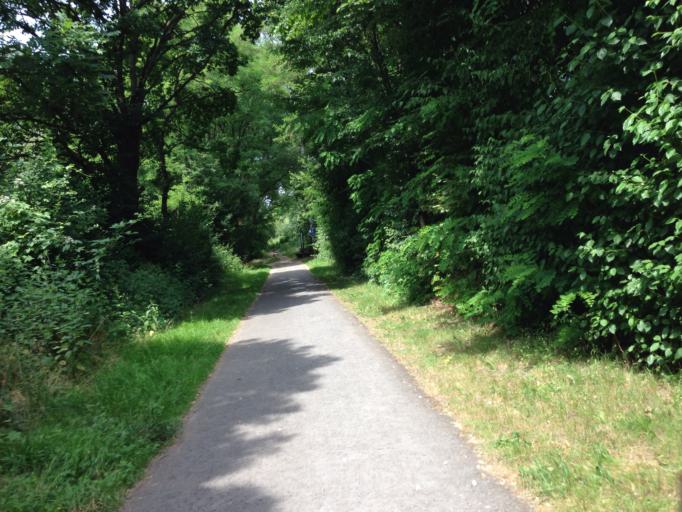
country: DE
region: Bavaria
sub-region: Regierungsbezirk Unterfranken
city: Kahl am Main
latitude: 50.0665
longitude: 8.9926
